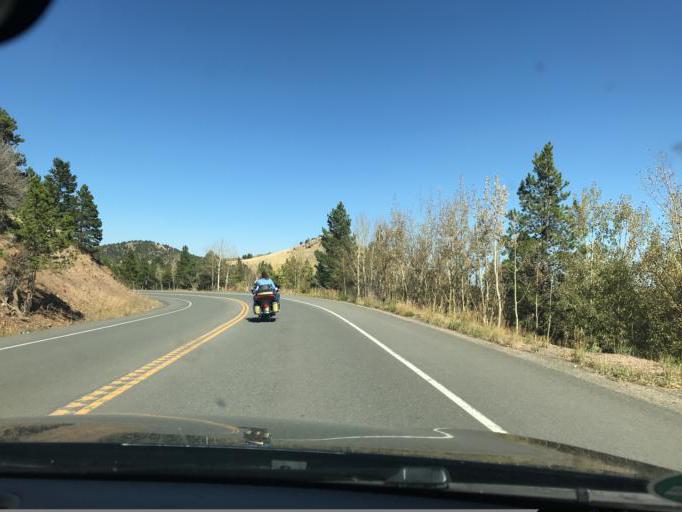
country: US
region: Colorado
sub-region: Boulder County
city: Nederland
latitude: 40.0550
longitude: -105.5241
